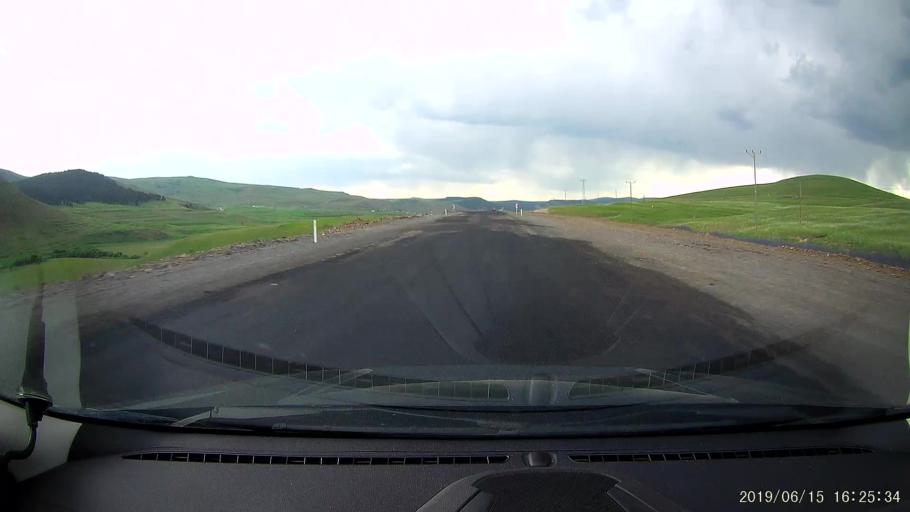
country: TR
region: Ardahan
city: Hanak
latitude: 41.1524
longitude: 42.8686
